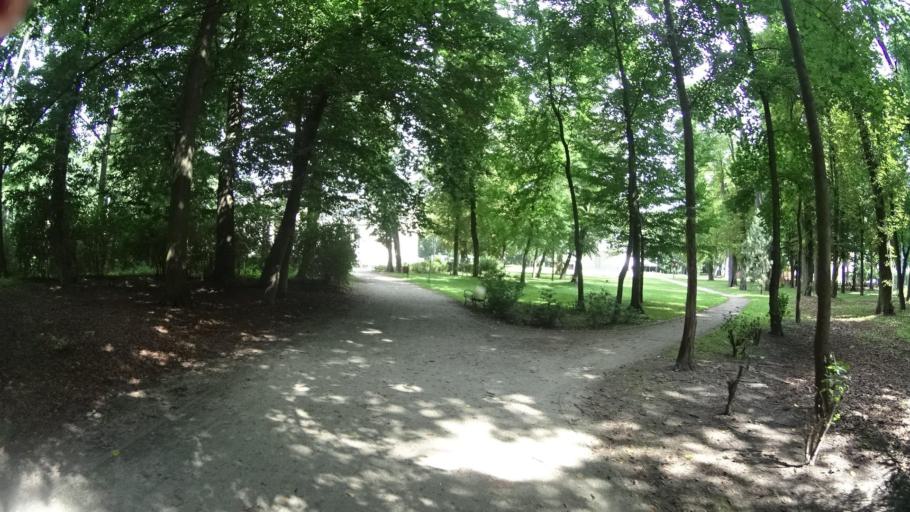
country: PL
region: Masovian Voivodeship
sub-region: Powiat pruszkowski
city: Nadarzyn
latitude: 52.0468
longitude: 20.7836
